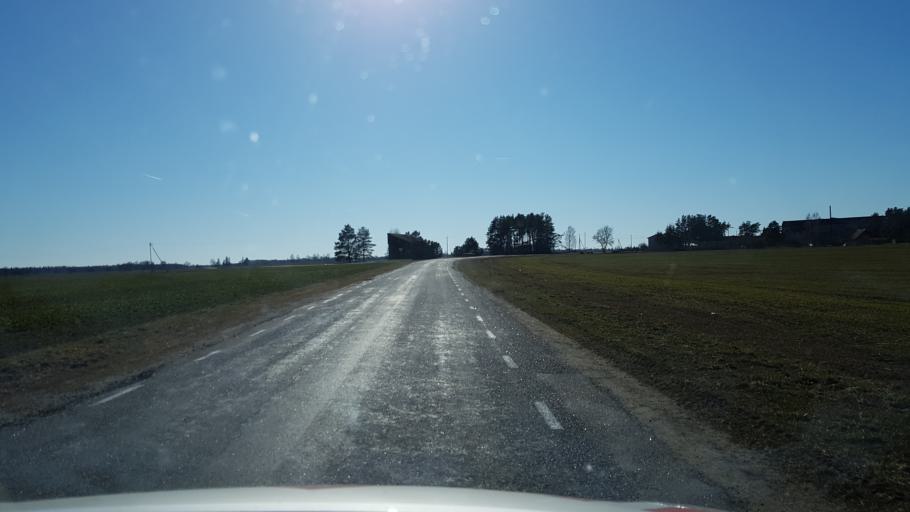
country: EE
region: Laeaene-Virumaa
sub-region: Haljala vald
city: Haljala
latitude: 59.4336
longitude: 26.2481
